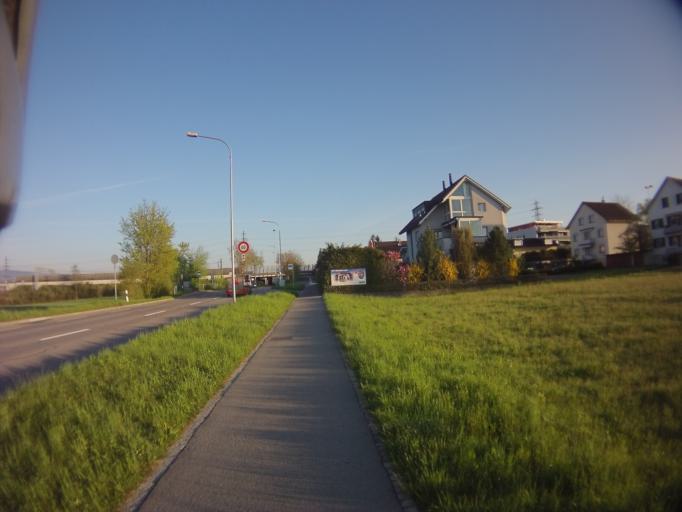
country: CH
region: Zug
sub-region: Zug
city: Cham
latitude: 47.1934
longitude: 8.4553
